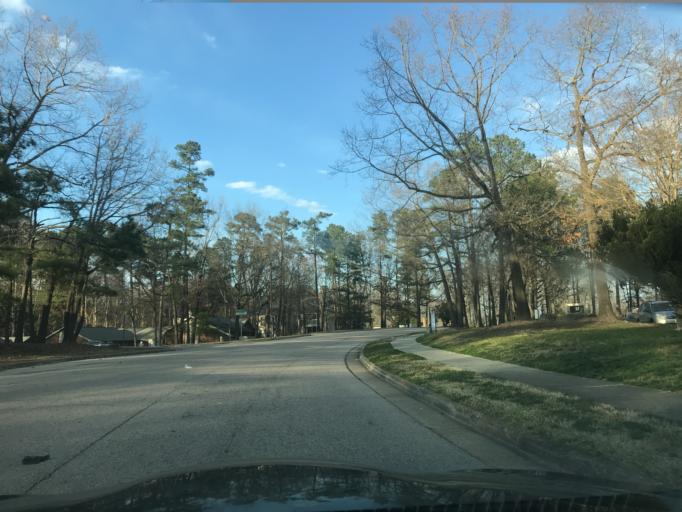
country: US
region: North Carolina
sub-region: Wake County
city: Raleigh
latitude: 35.8501
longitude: -78.5735
